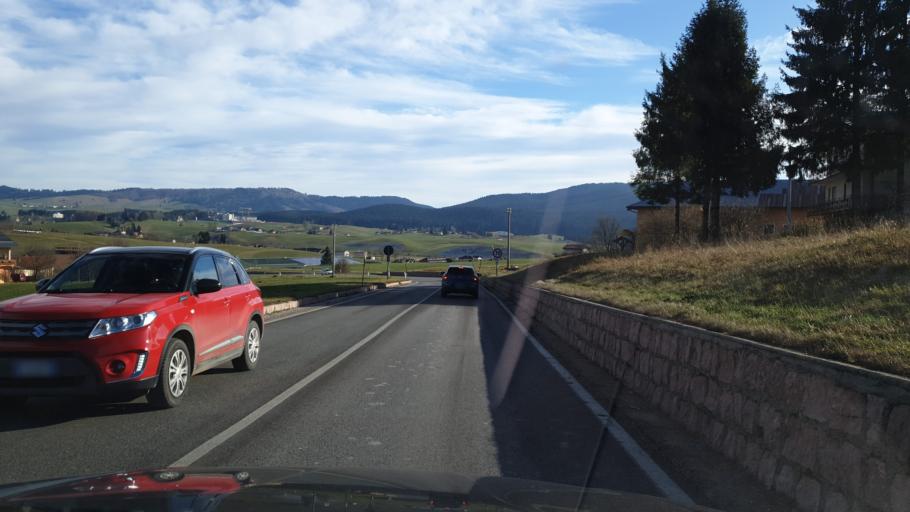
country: IT
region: Veneto
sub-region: Provincia di Vicenza
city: Canove di Roana
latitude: 45.8687
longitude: 11.4916
